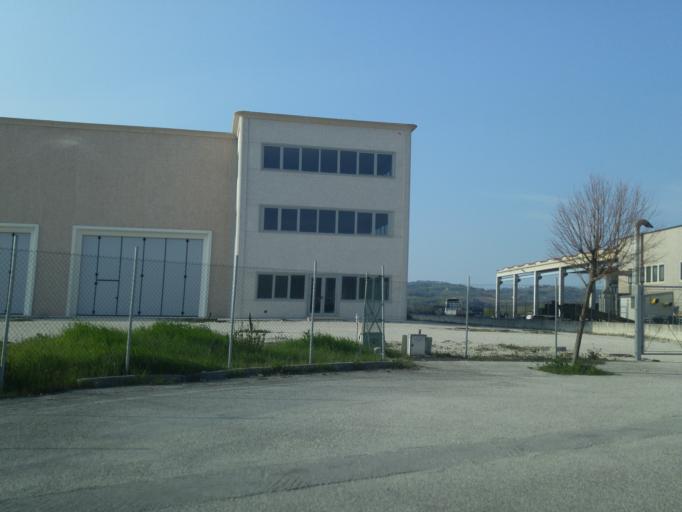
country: IT
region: The Marches
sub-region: Provincia di Pesaro e Urbino
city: Tavernelle
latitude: 43.7172
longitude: 12.8943
